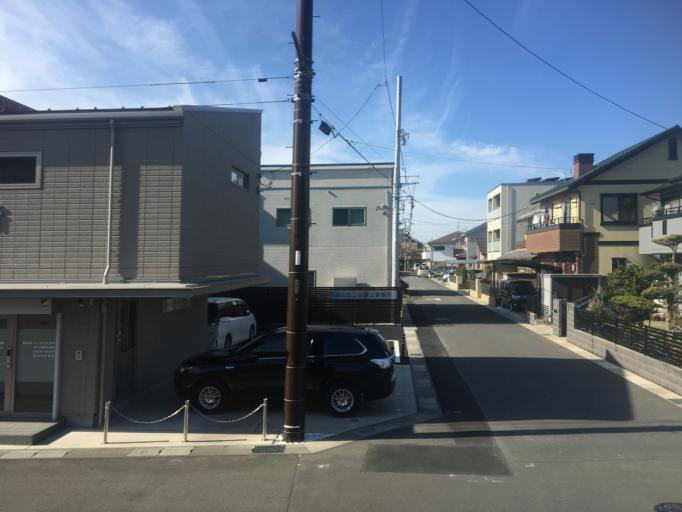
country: JP
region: Saitama
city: Sakado
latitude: 35.9469
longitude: 139.4112
